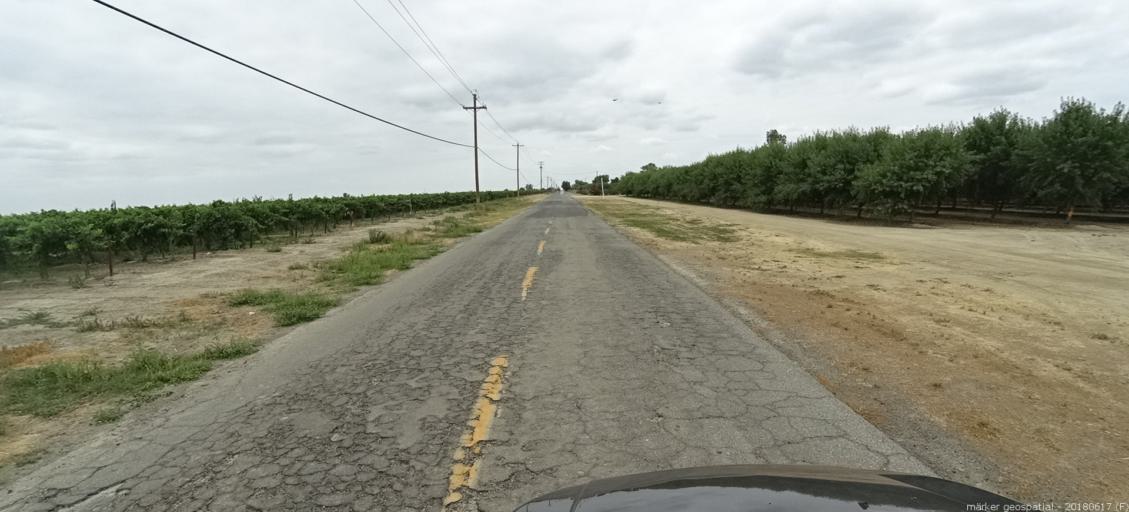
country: US
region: California
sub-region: Madera County
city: Madera
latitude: 36.9079
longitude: -120.1652
